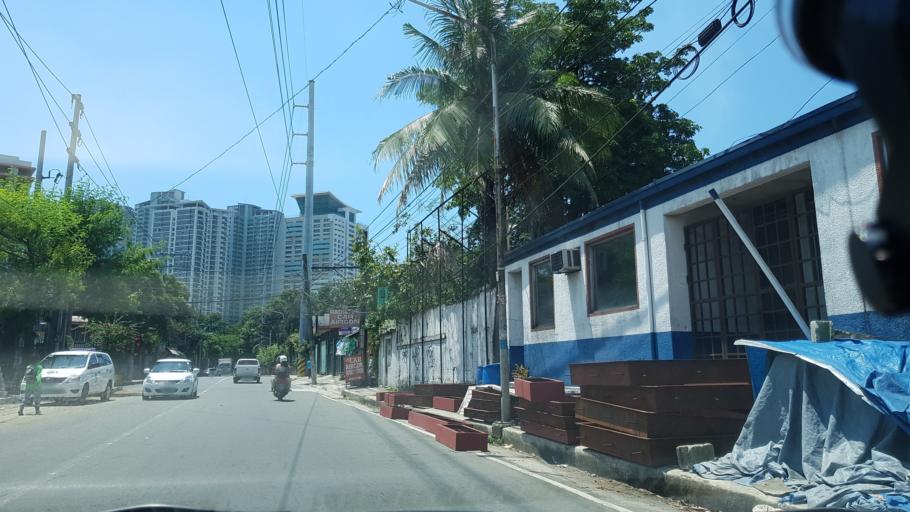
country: PH
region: Metro Manila
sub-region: San Juan
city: San Juan
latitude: 14.6169
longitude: 121.0437
